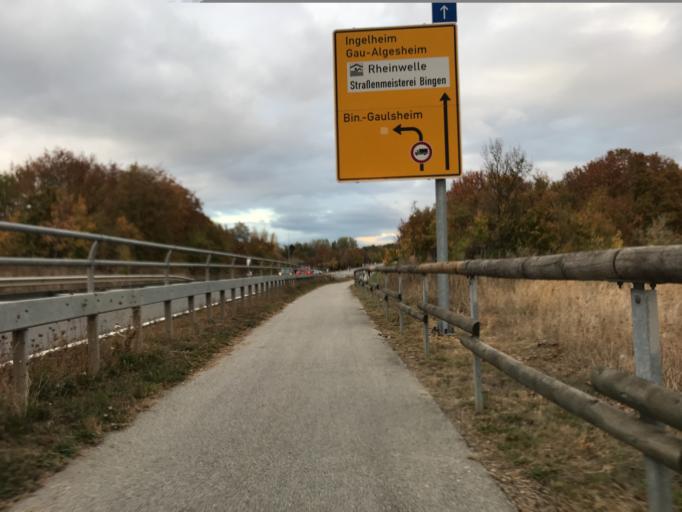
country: DE
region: Hesse
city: Geisenheim
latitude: 49.9644
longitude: 7.9687
